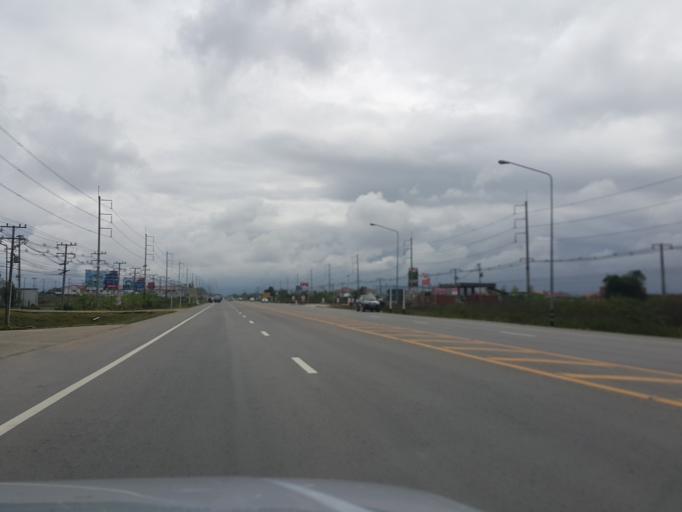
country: TH
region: Chiang Mai
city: San Kamphaeng
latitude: 18.7422
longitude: 99.0785
